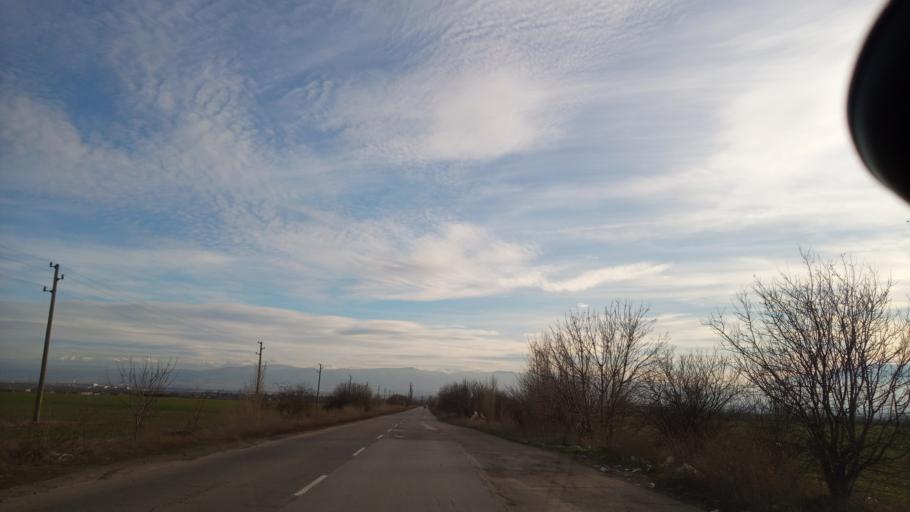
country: BG
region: Sofia-Capital
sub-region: Stolichna Obshtina
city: Bukhovo
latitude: 42.7504
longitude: 23.5574
